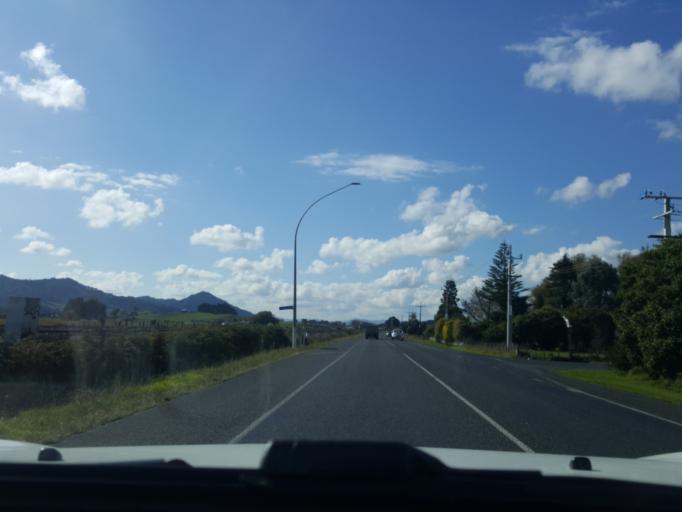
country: NZ
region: Waikato
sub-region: Waikato District
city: Ngaruawahia
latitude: -37.6544
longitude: 175.1554
